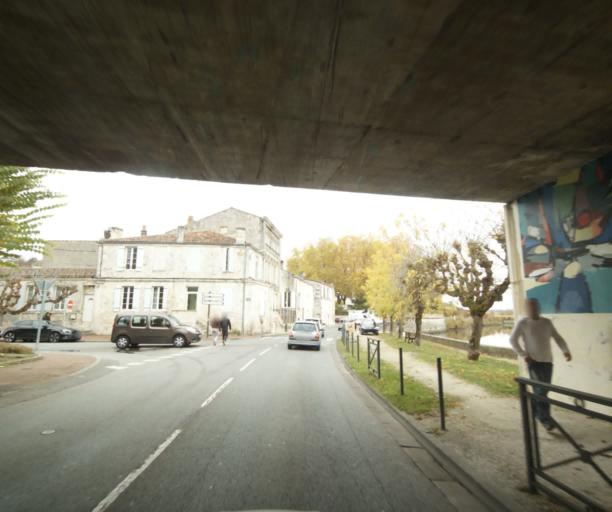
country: FR
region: Poitou-Charentes
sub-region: Departement de la Charente-Maritime
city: Saintes
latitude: 45.7418
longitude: -0.6369
